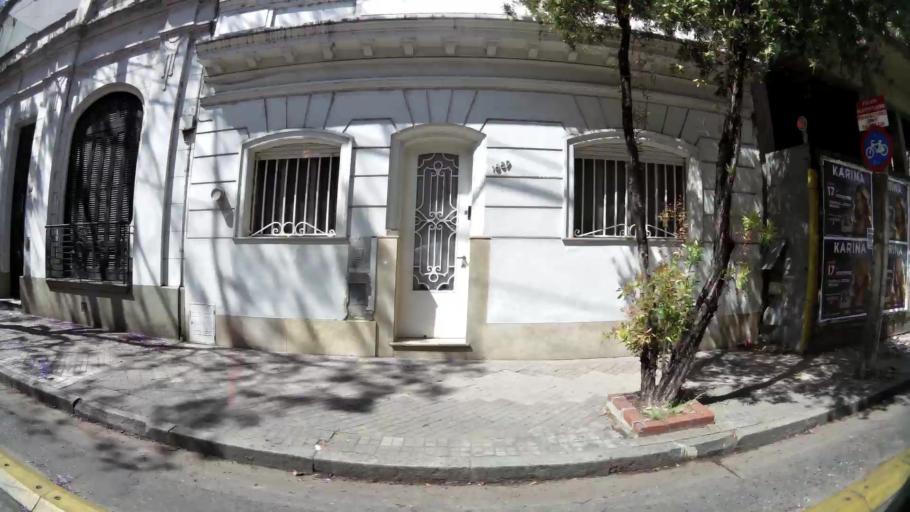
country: AR
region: Santa Fe
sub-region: Departamento de Rosario
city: Rosario
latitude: -32.9387
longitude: -60.6476
